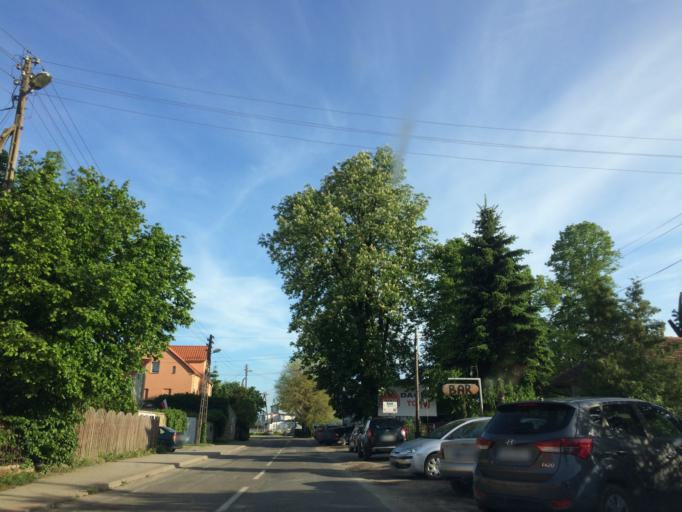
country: PL
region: Lower Silesian Voivodeship
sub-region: Powiat swidnicki
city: Swidnica
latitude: 50.8257
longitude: 16.4890
